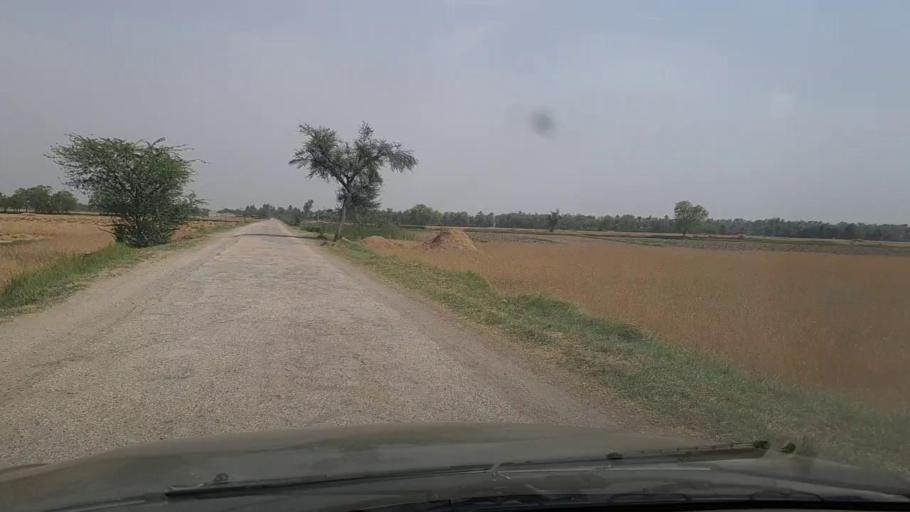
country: PK
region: Sindh
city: Lakhi
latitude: 27.8469
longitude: 68.7560
